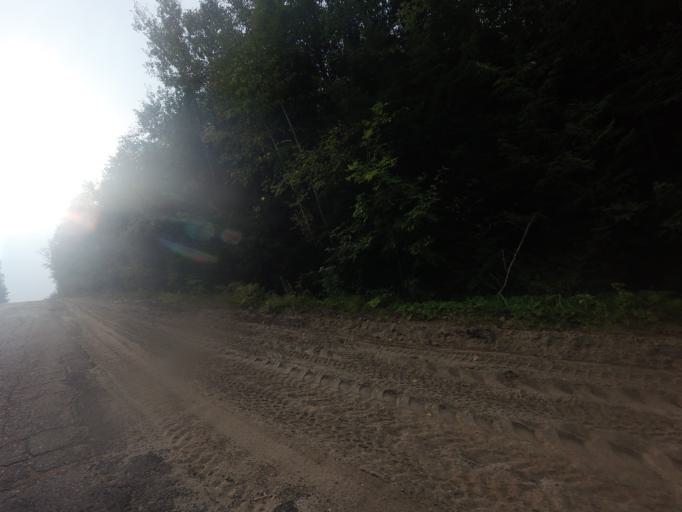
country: CA
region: Quebec
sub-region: Outaouais
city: Maniwaki
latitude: 46.0848
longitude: -76.0302
